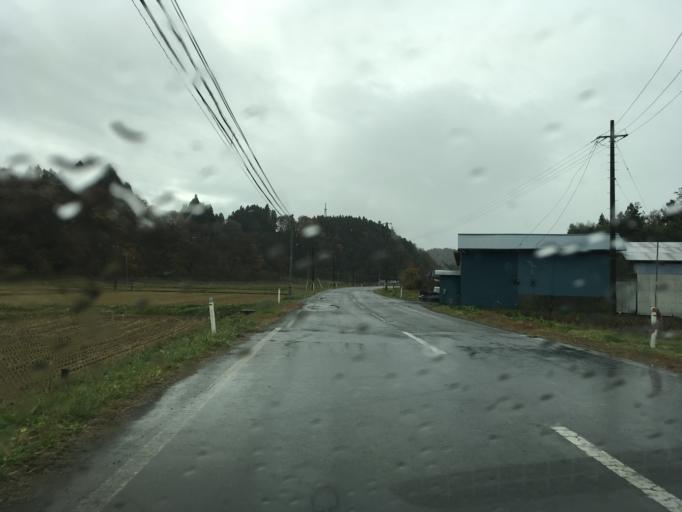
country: JP
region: Iwate
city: Ichinoseki
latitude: 38.8007
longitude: 141.2492
